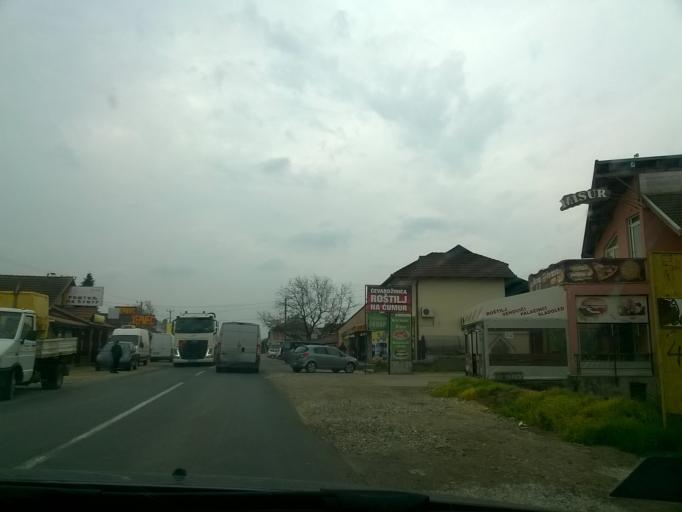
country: RS
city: Platicevo
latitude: 44.8247
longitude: 19.7803
